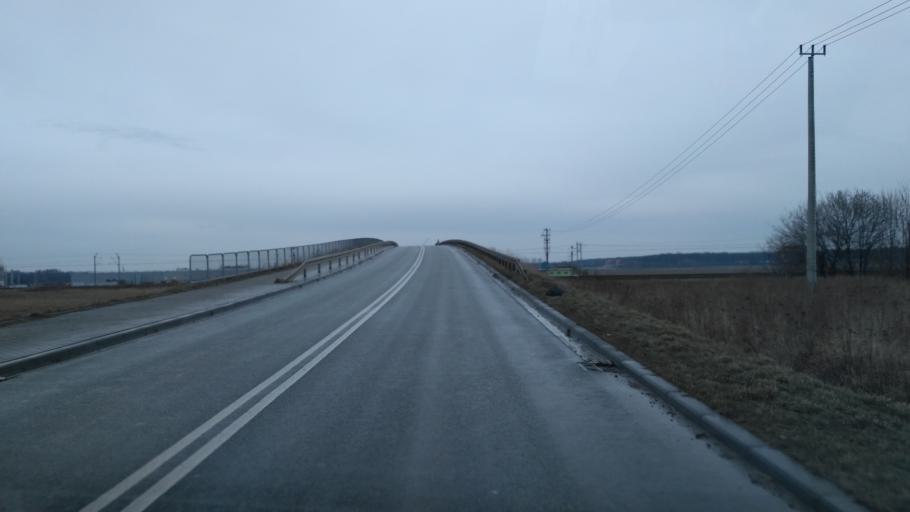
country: PL
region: Subcarpathian Voivodeship
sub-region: Powiat debicki
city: Brzeznica
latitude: 50.0640
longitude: 21.4760
